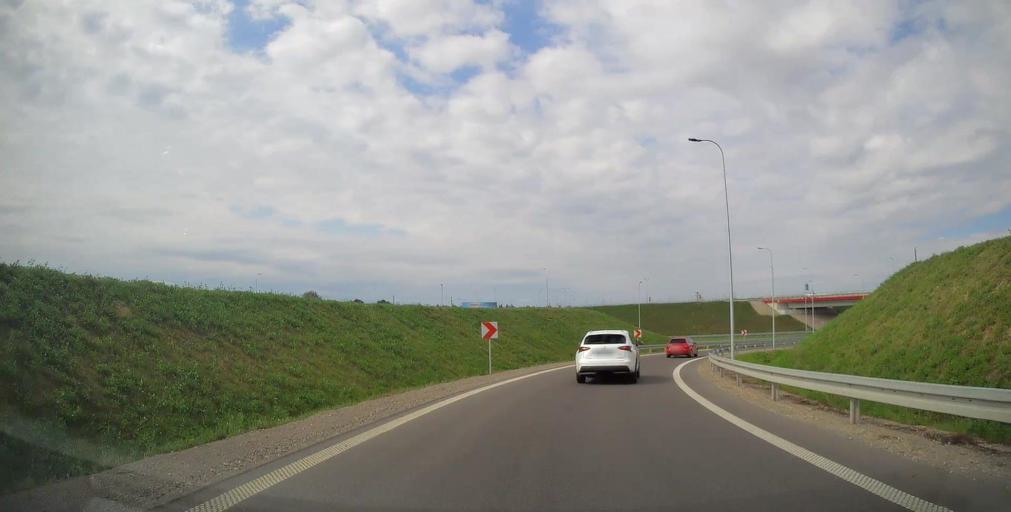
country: PL
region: Lesser Poland Voivodeship
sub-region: Powiat krakowski
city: Michalowice
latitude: 50.2065
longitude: 20.0197
